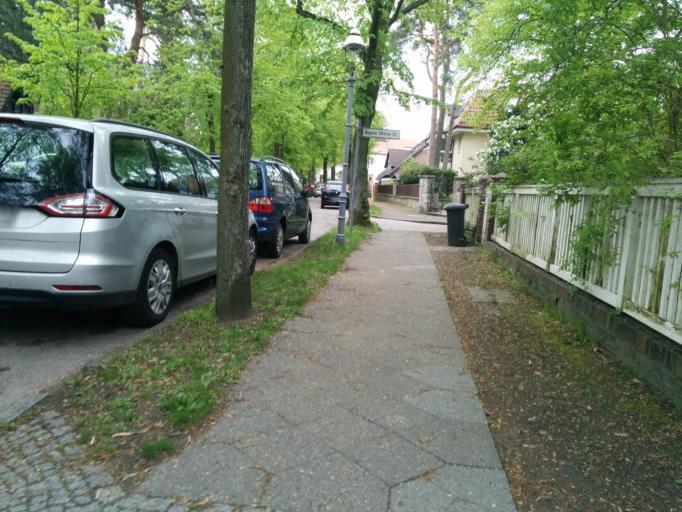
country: DE
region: Berlin
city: Hermsdorf
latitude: 52.6212
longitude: 13.3157
